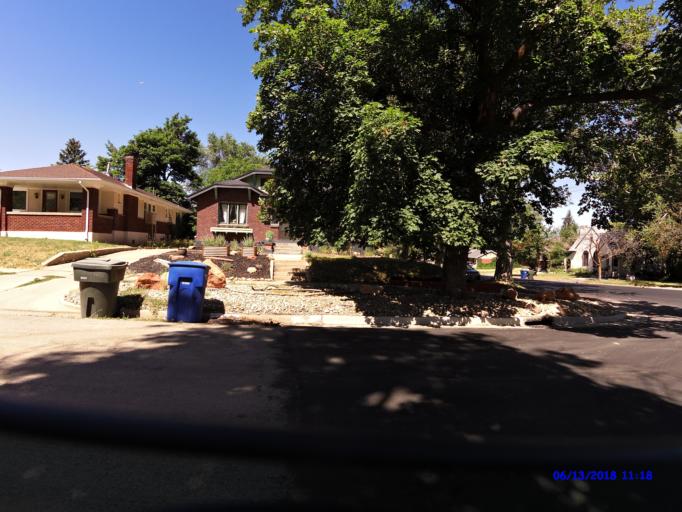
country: US
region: Utah
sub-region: Weber County
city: Ogden
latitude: 41.2160
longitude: -111.9498
